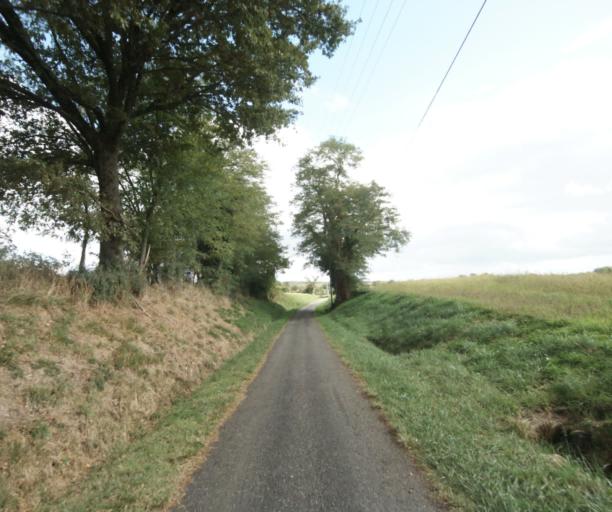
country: FR
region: Midi-Pyrenees
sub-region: Departement du Gers
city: Cazaubon
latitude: 43.8552
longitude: -0.0255
